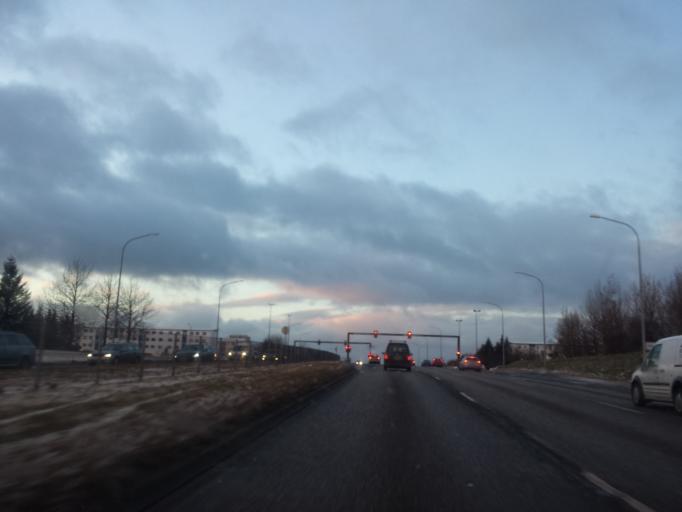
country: IS
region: Capital Region
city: Reykjavik
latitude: 64.1305
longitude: -21.8808
